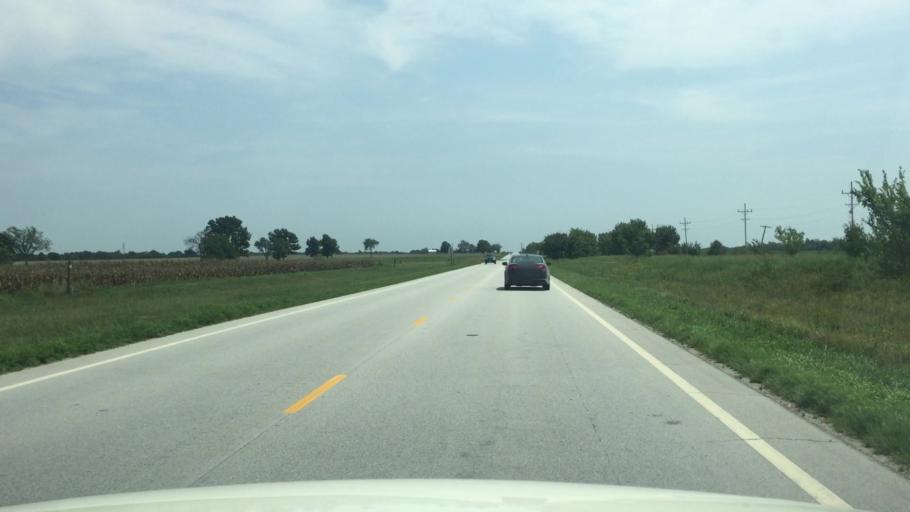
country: US
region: Kansas
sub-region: Cherokee County
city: Columbus
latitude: 37.1792
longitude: -94.9246
